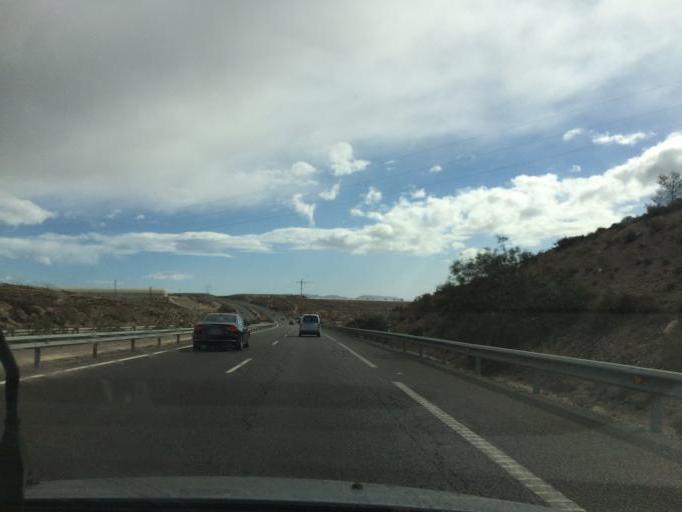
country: ES
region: Andalusia
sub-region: Provincia de Almeria
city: Retamar
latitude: 36.8694
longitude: -2.3205
